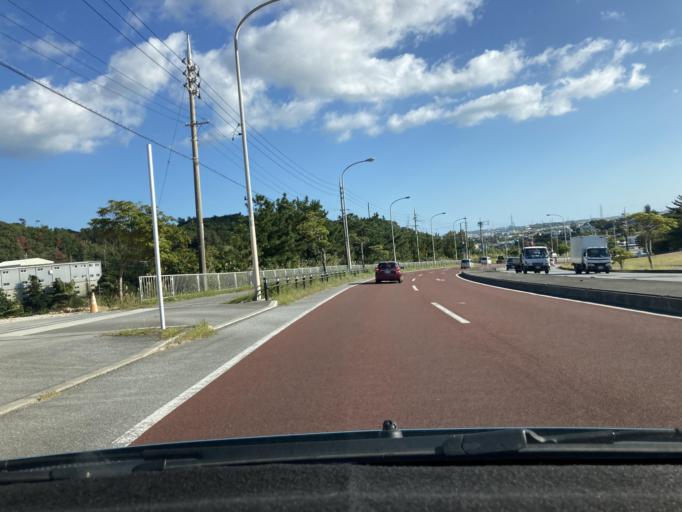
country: JP
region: Okinawa
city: Ishikawa
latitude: 26.4012
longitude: 127.8281
